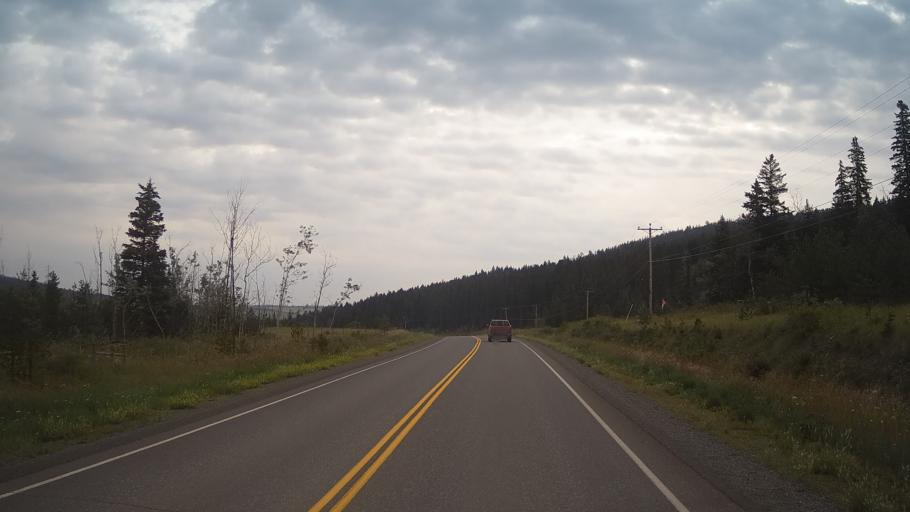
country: CA
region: British Columbia
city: Hanceville
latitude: 51.9606
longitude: -122.6824
